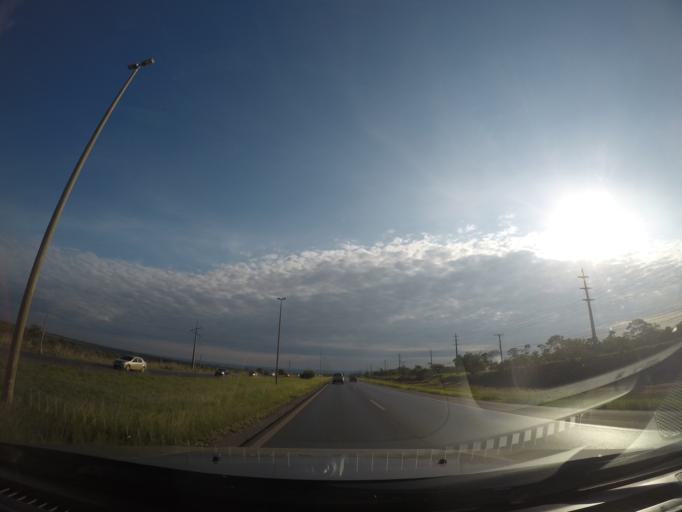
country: BR
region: Goias
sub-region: Planaltina
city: Planaltina
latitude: -15.6357
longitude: -47.7425
